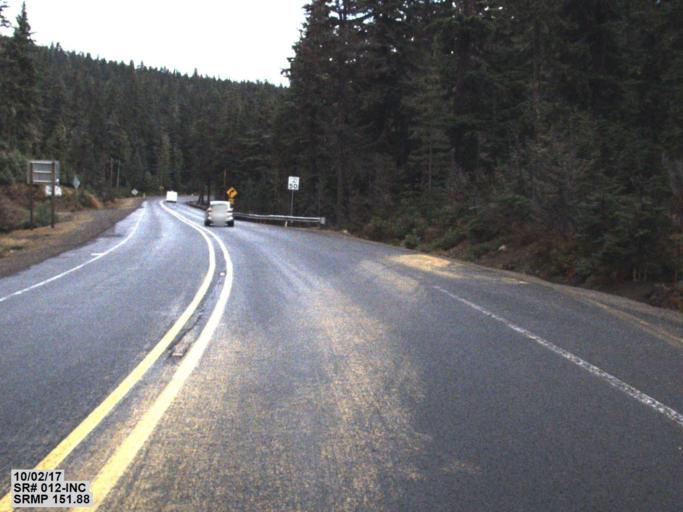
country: US
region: Washington
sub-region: Yakima County
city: Tieton
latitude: 46.6457
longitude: -121.3770
